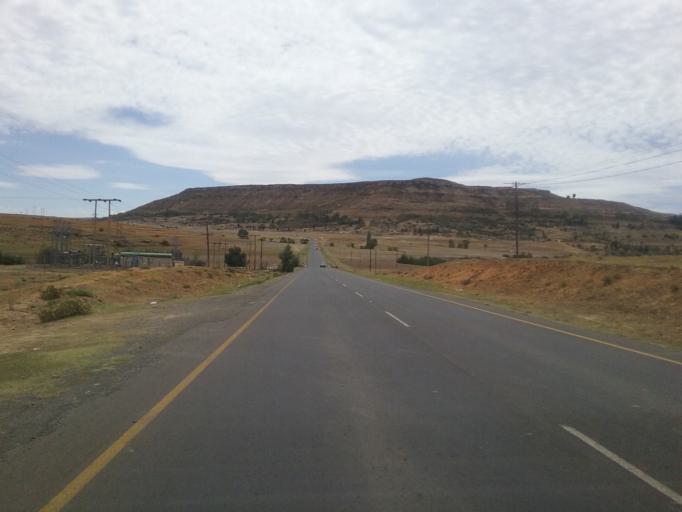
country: LS
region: Maseru
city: Nako
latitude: -29.6178
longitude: 27.4982
